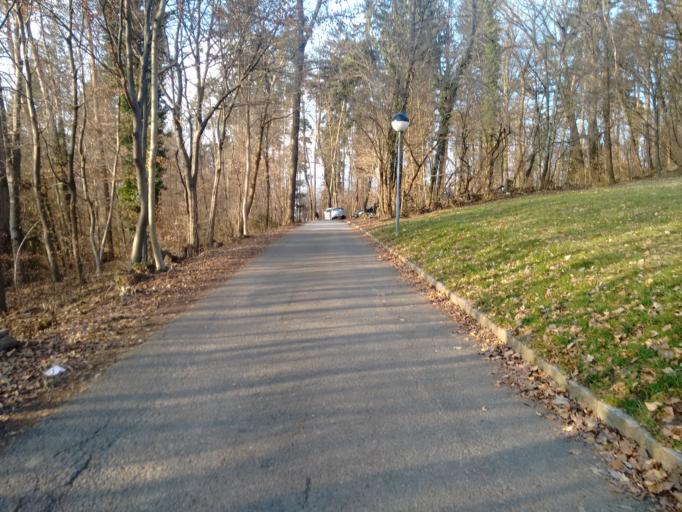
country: AT
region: Styria
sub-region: Graz Stadt
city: Mariatrost
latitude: 47.0685
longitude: 15.4924
